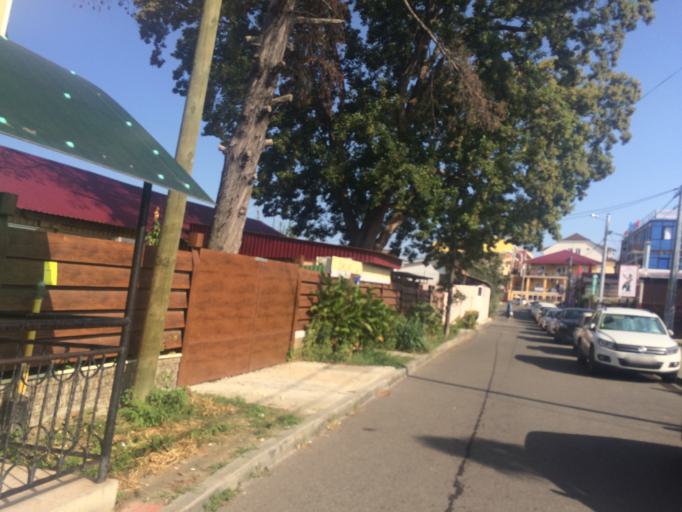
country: RU
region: Krasnodarskiy
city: Adler
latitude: 43.3929
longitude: 39.9861
